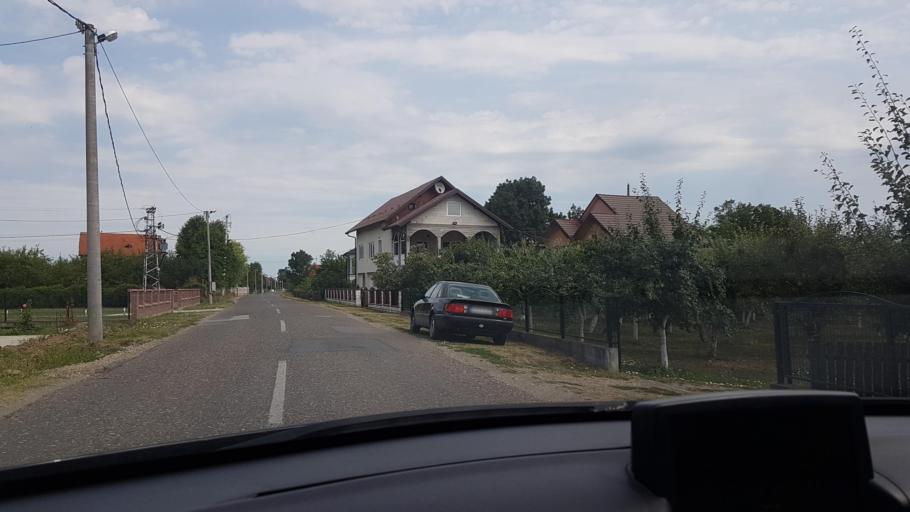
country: BA
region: Republika Srpska
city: Dvorovi
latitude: 44.8142
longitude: 19.2175
